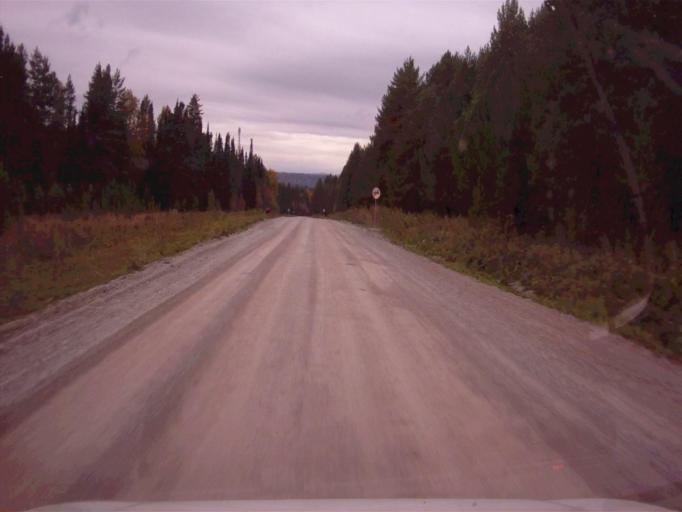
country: RU
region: Chelyabinsk
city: Nyazepetrovsk
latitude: 56.0529
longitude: 59.5348
